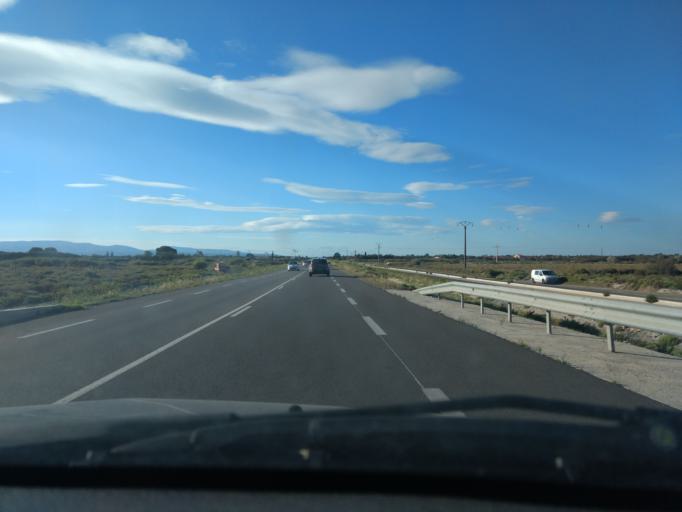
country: FR
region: Languedoc-Roussillon
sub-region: Departement des Pyrenees-Orientales
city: Torreilles
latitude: 42.7538
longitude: 3.0212
